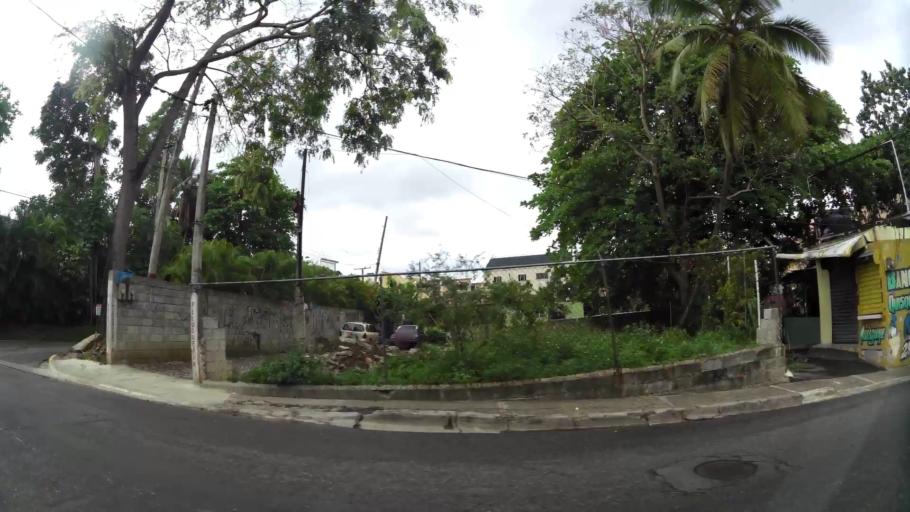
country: DO
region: Nacional
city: La Agustina
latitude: 18.5047
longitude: -69.9441
